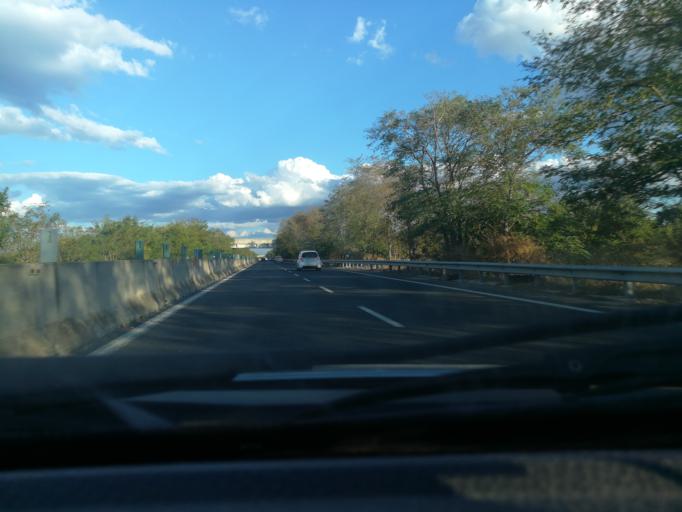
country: IT
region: Apulia
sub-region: Provincia di Bari
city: Mola di Bari
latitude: 41.0418
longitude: 17.1143
